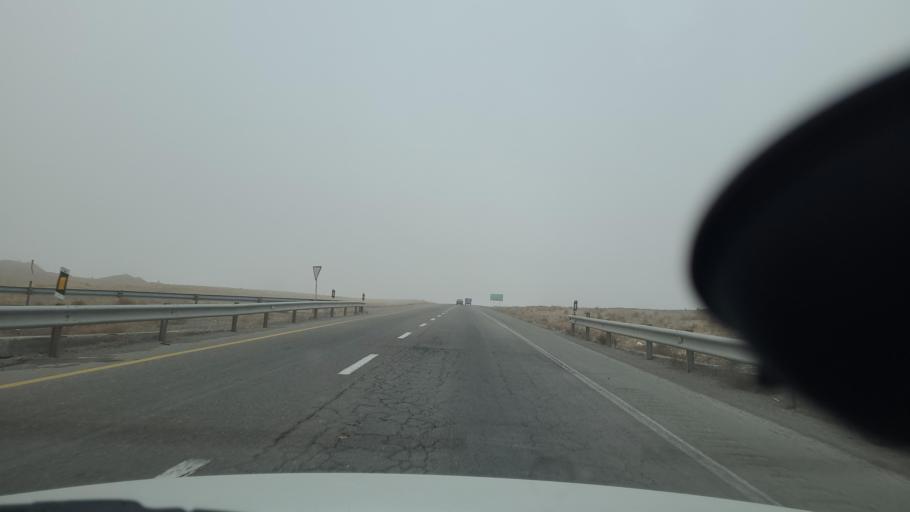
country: IR
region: Razavi Khorasan
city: Fariman
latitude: 35.8244
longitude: 59.7475
